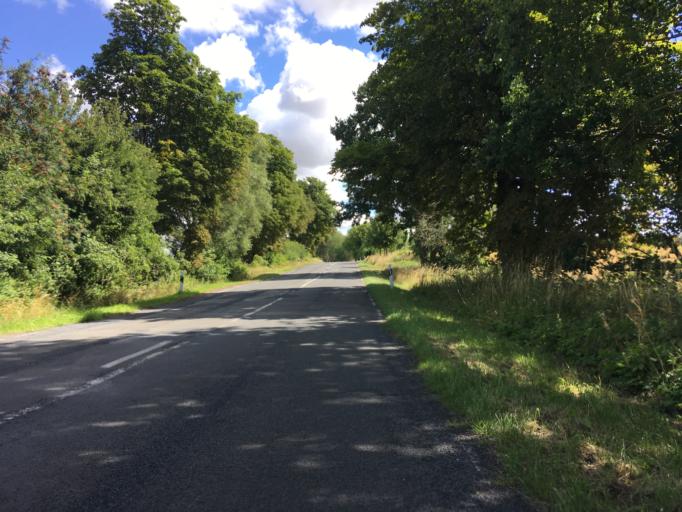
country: DE
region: Brandenburg
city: Mittenwalde
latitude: 53.1860
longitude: 13.5869
